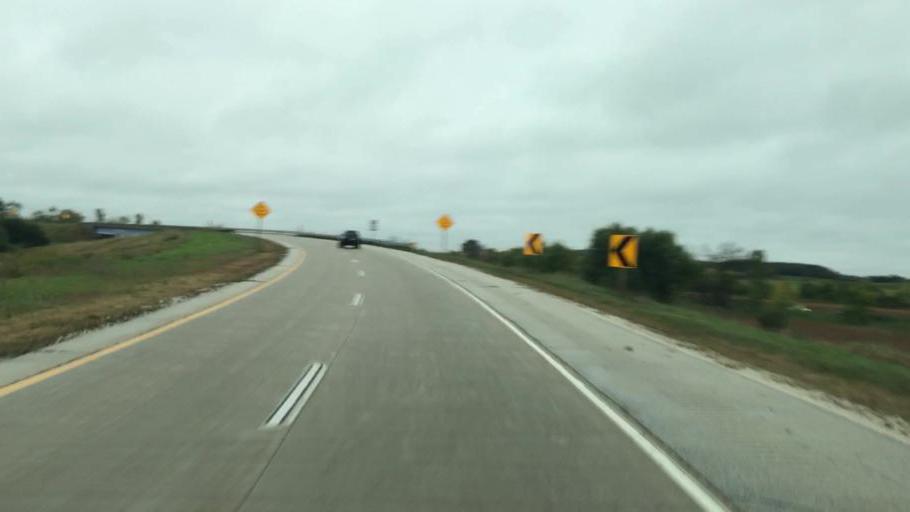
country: US
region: Wisconsin
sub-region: Waukesha County
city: Pewaukee
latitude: 43.0487
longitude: -88.2506
